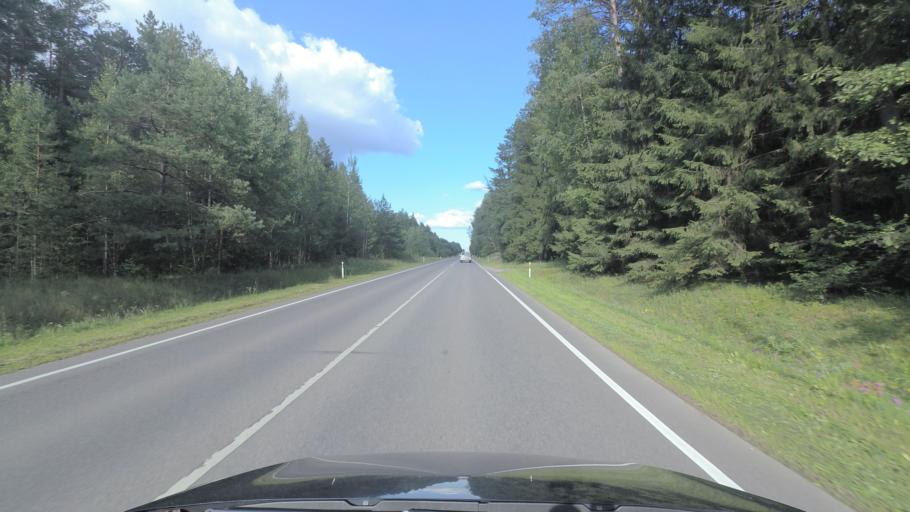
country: LT
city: Pabrade
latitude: 54.9707
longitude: 25.7285
